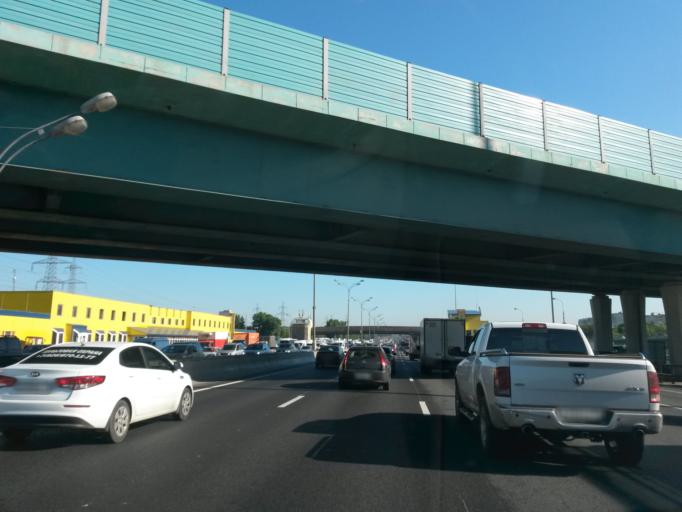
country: RU
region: Moskovskaya
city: Kuskovo
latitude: 55.7304
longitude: 37.8405
